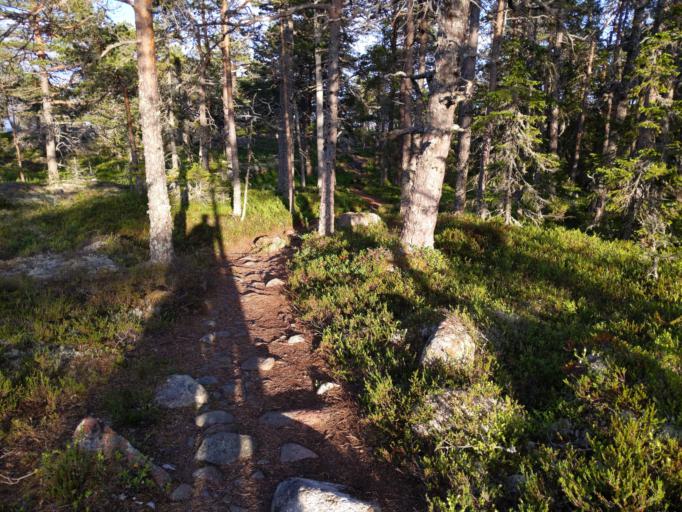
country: SE
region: Vaesternorrland
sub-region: OErnskoeldsviks Kommun
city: Ornskoldsvik
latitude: 63.1671
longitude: 18.7171
